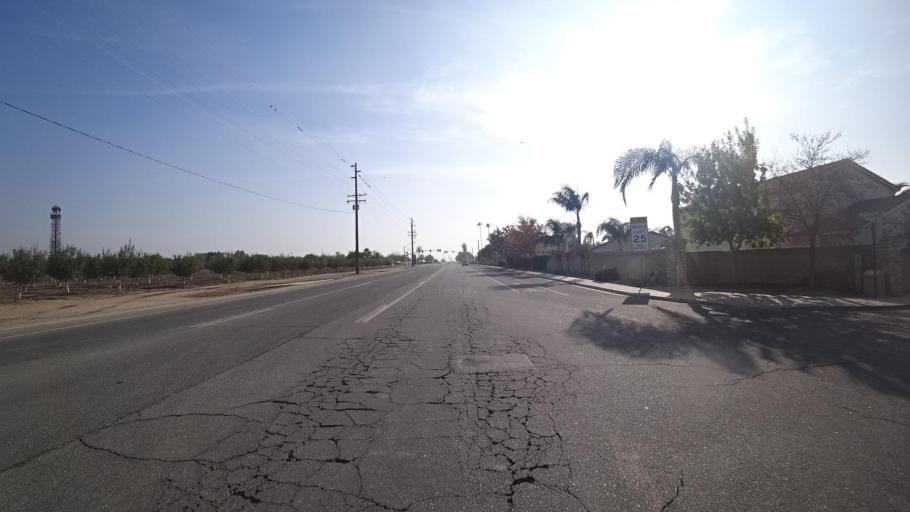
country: US
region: California
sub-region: Kern County
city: Delano
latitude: 35.7704
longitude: -119.2233
